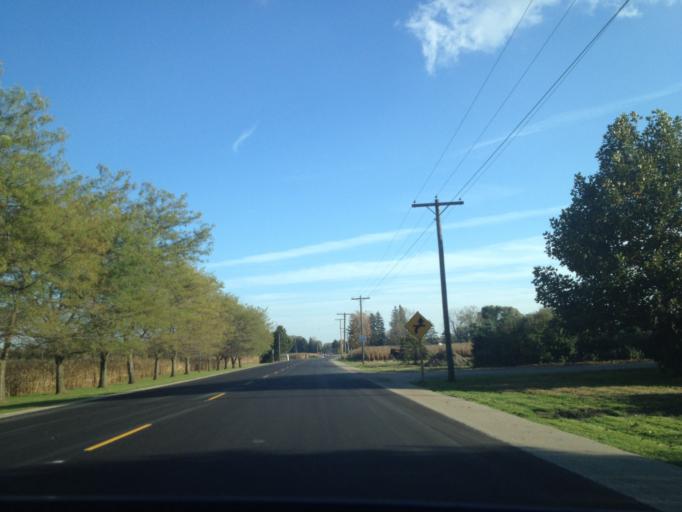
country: CA
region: Ontario
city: Delaware
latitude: 42.5886
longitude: -81.5879
